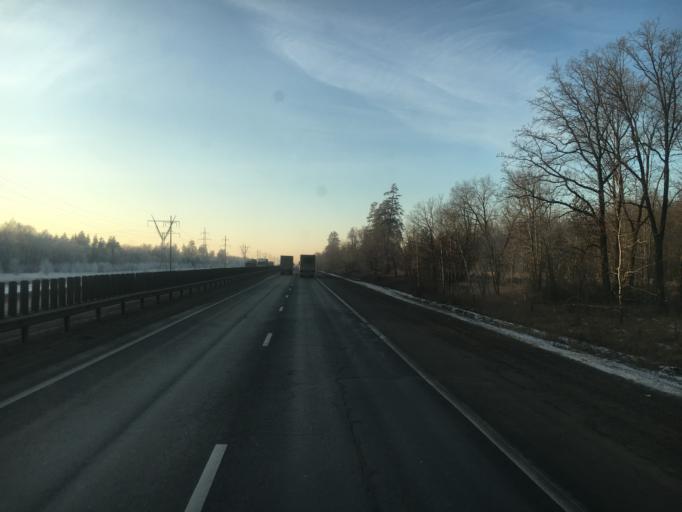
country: RU
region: Samara
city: Pribrezhnyy
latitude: 53.5160
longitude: 49.8653
